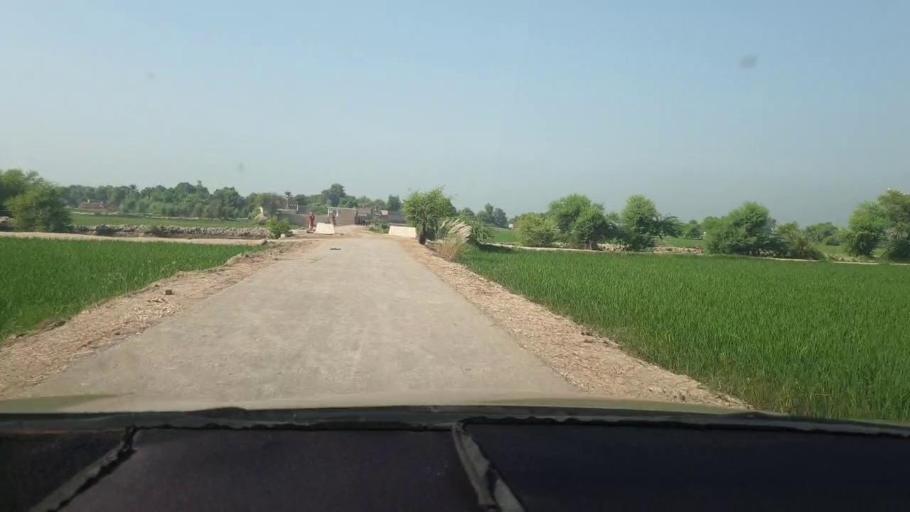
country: PK
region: Sindh
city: Kambar
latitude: 27.5718
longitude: 68.0857
